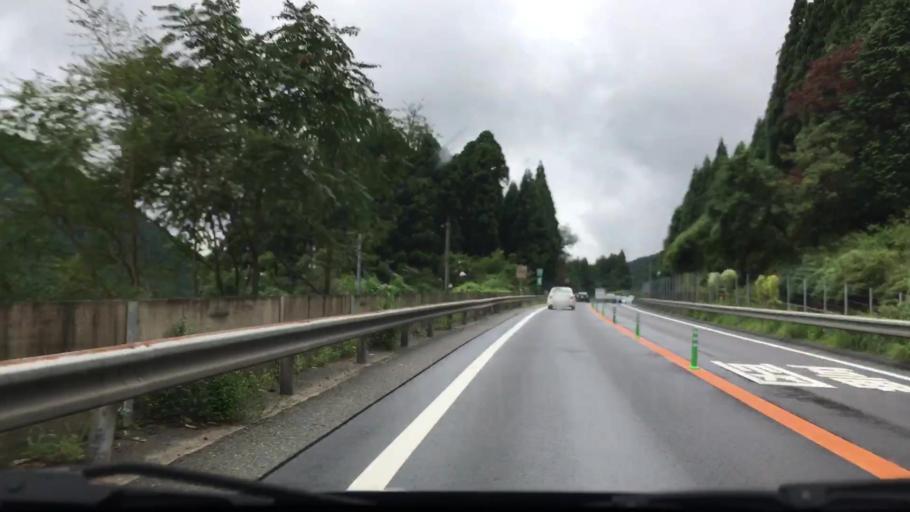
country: JP
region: Hyogo
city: Nishiwaki
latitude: 35.1136
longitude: 134.7836
